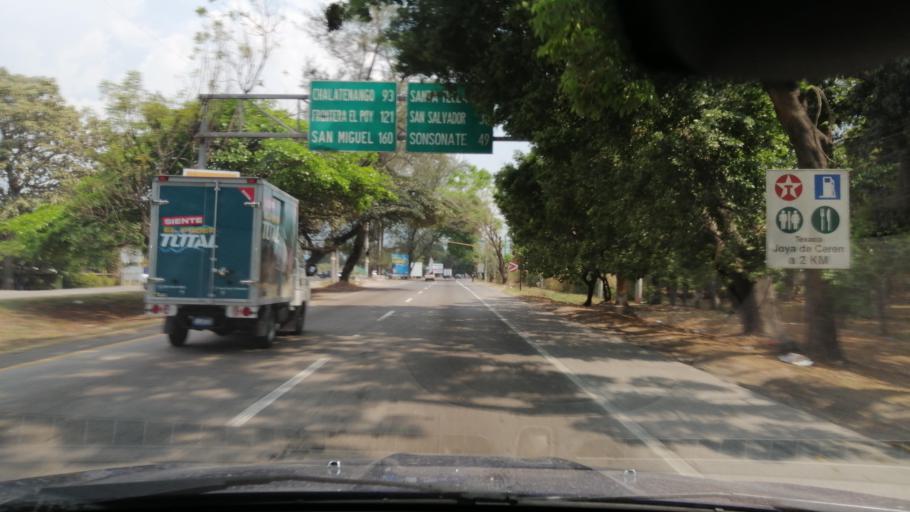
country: SV
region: La Libertad
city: Ciudad Arce
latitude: 13.7834
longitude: -89.3767
